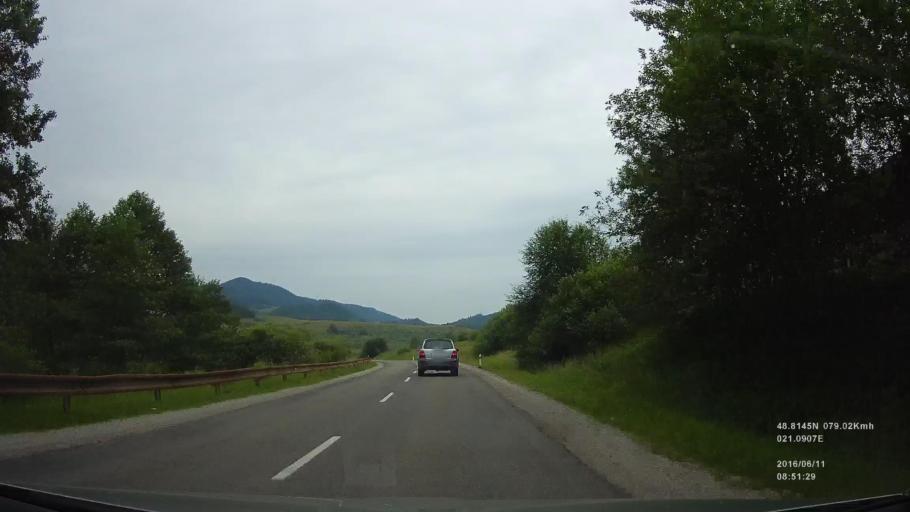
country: SK
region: Kosicky
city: Gelnica
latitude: 48.8089
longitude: 21.0970
